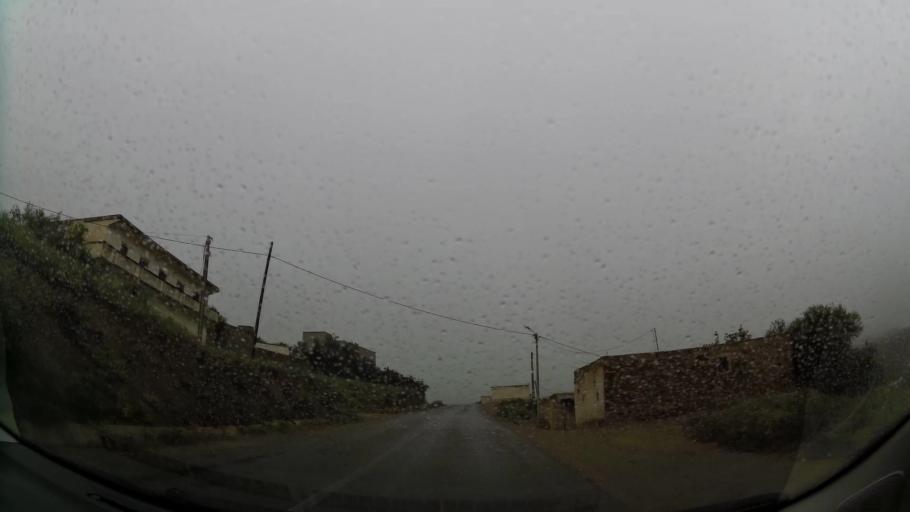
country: MA
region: Oriental
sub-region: Nador
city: Boudinar
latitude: 35.0939
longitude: -3.5260
